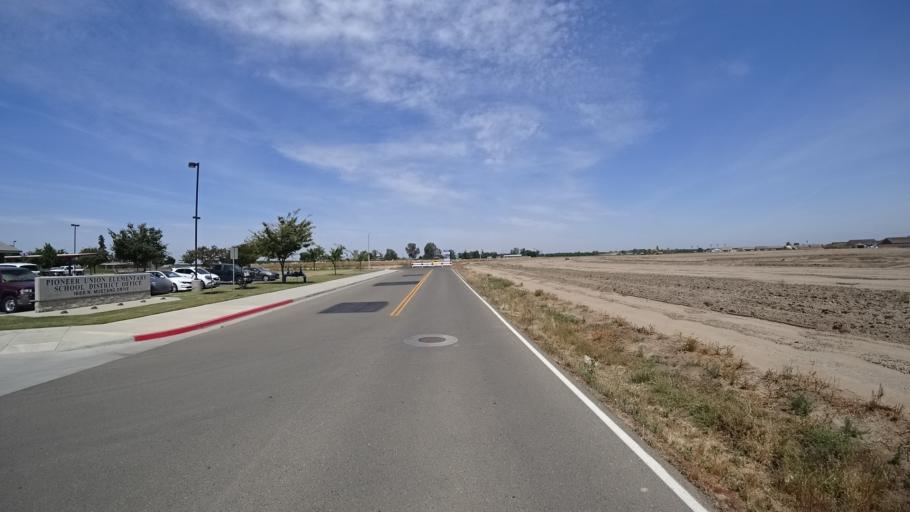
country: US
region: California
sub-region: Kings County
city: Armona
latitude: 36.3459
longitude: -119.6870
